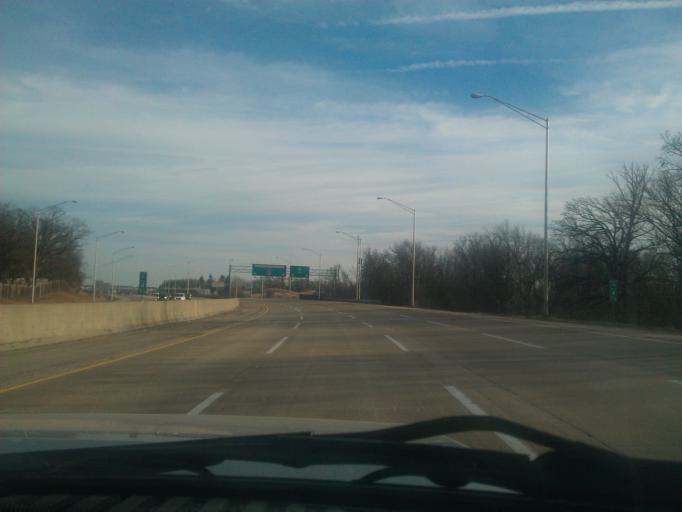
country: US
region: Illinois
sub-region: Lake County
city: Wadsworth
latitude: 42.4367
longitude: -87.9555
